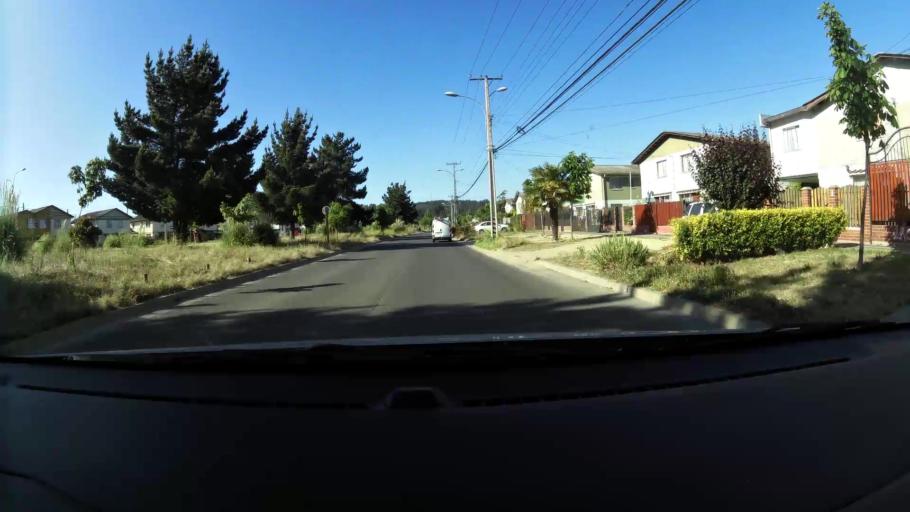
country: CL
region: Valparaiso
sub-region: Provincia de Valparaiso
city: Valparaiso
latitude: -33.1182
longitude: -71.5792
